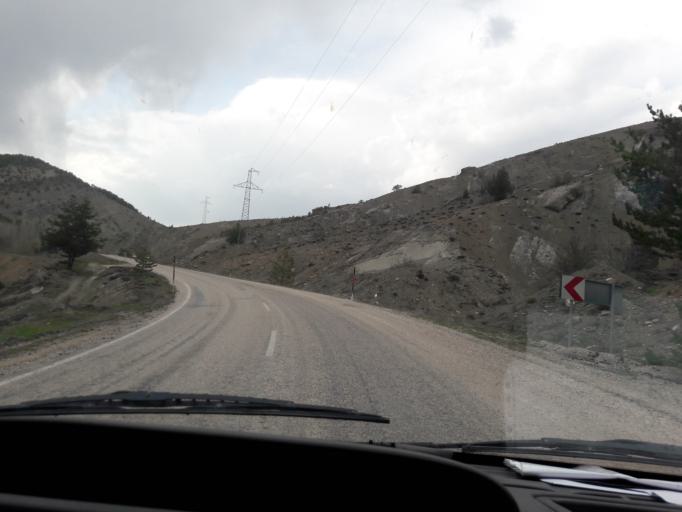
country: TR
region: Giresun
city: Alucra
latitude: 40.2800
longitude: 38.8236
